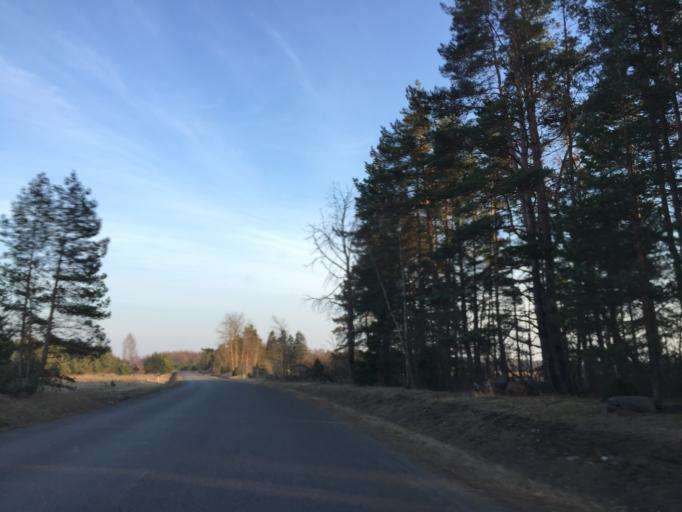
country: EE
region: Laeaene
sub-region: Lihula vald
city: Lihula
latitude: 58.4657
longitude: 23.7229
